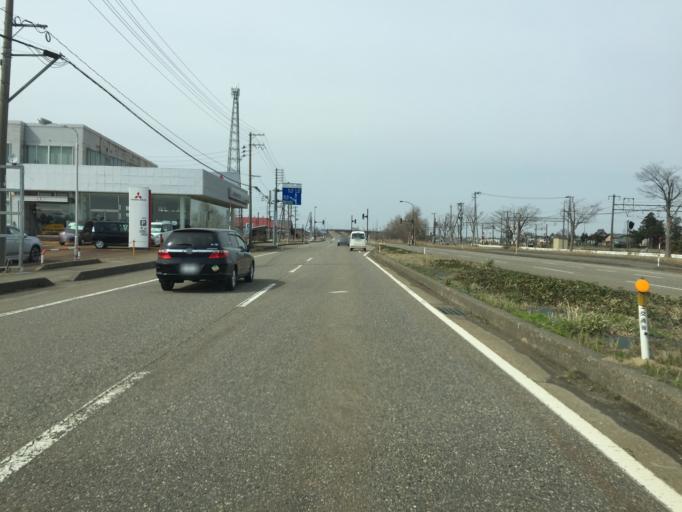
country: JP
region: Niigata
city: Nagaoka
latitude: 37.3803
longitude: 138.8345
